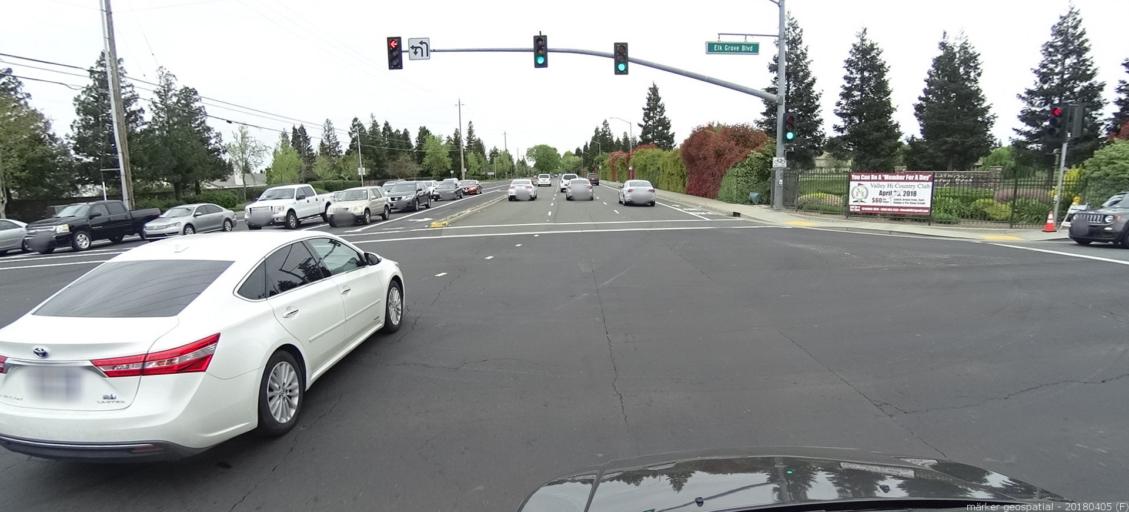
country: US
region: California
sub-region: Sacramento County
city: Laguna
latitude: 38.4087
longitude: -121.4498
